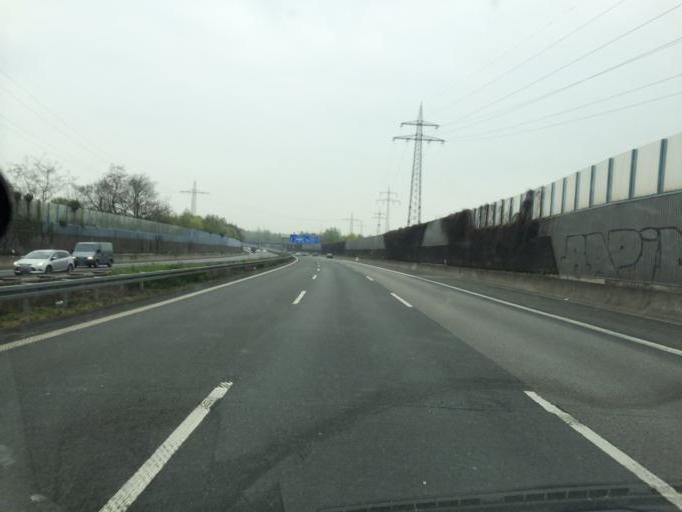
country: DE
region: North Rhine-Westphalia
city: Castrop-Rauxel
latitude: 51.5929
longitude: 7.3446
